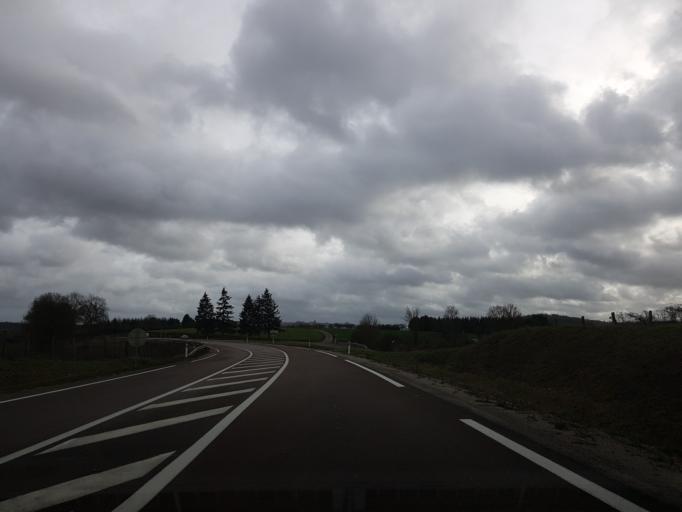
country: FR
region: Champagne-Ardenne
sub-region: Departement de la Haute-Marne
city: Rolampont
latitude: 47.9086
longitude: 5.2931
